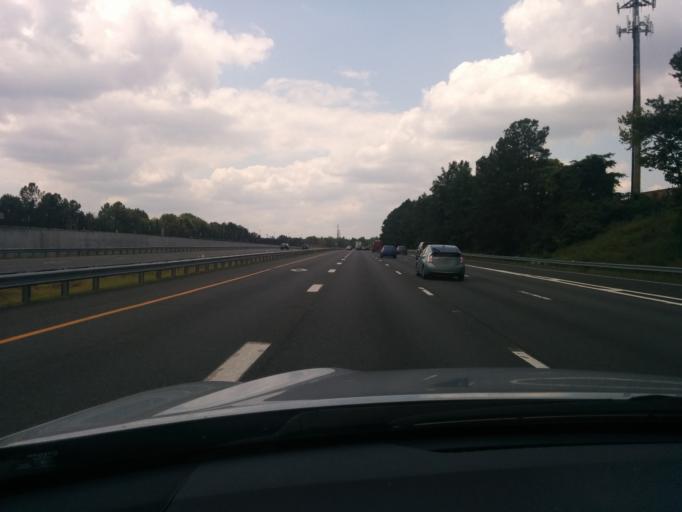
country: US
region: Virginia
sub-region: Fairfax County
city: Wolf Trap
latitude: 38.9471
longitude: -77.3157
